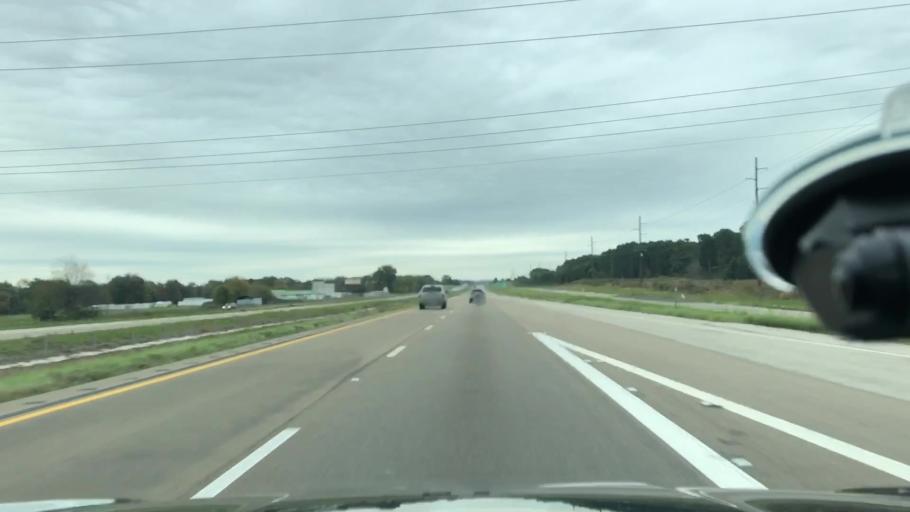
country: US
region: Texas
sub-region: Titus County
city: Mount Pleasant
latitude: 33.1592
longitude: -95.0696
